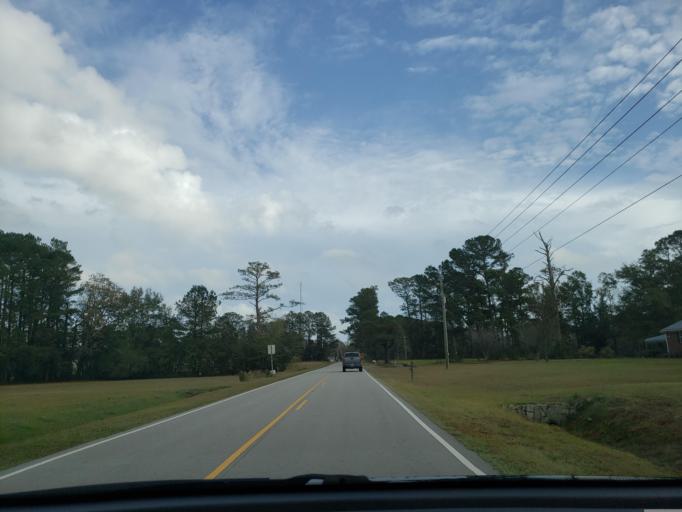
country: US
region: North Carolina
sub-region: Onslow County
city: Jacksonville
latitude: 34.6952
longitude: -77.5549
